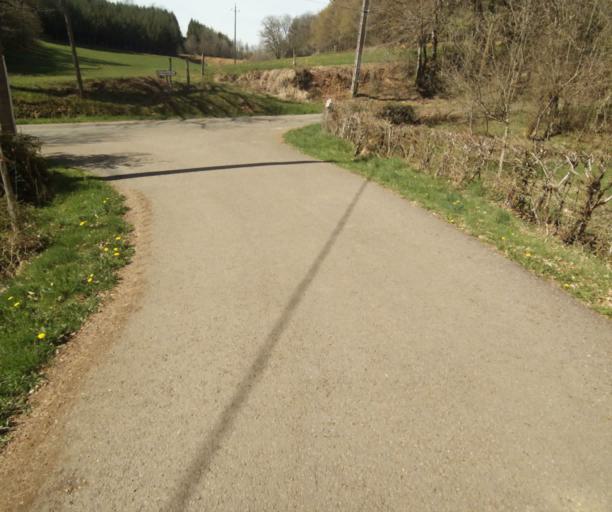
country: FR
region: Limousin
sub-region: Departement de la Correze
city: Seilhac
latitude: 45.4008
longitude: 1.7706
